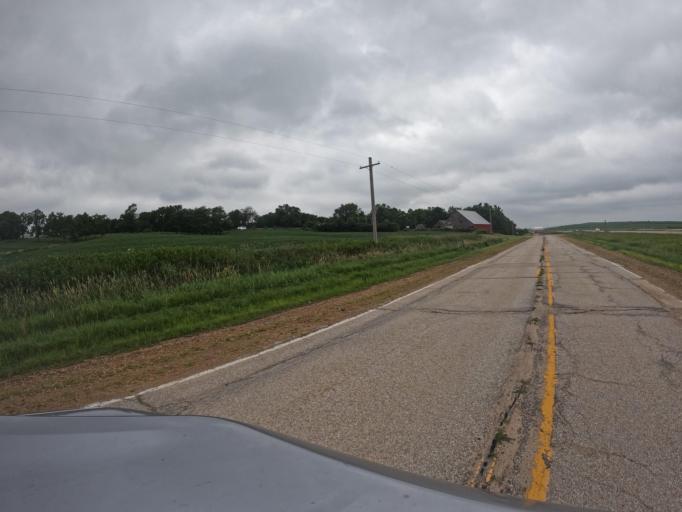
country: US
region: Iowa
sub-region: Clinton County
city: De Witt
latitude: 41.9227
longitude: -90.6034
